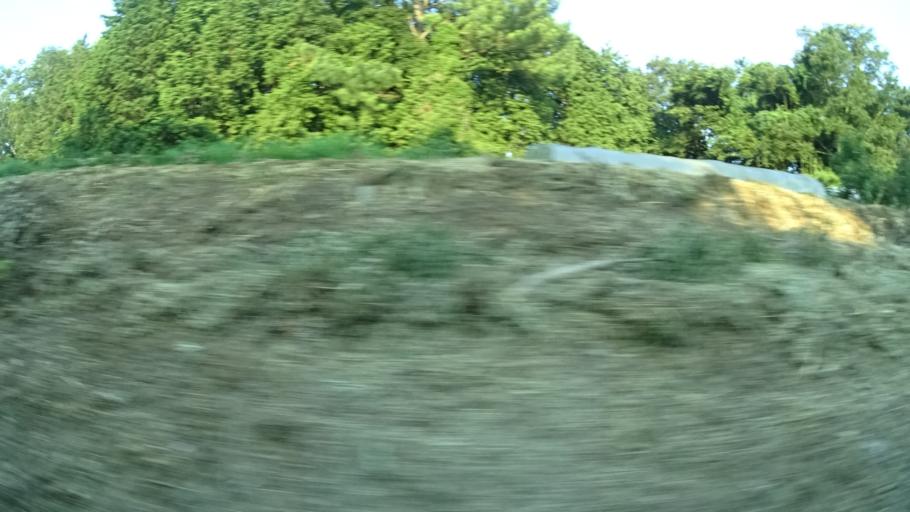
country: JP
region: Ibaraki
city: Ishioka
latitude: 36.1691
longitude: 140.2977
